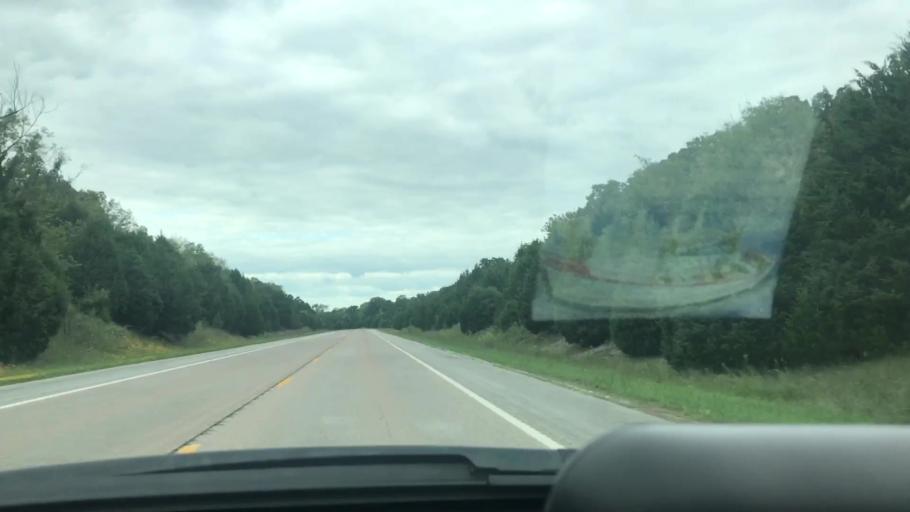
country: US
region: Missouri
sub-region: Benton County
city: Warsaw
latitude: 38.1998
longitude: -93.3256
